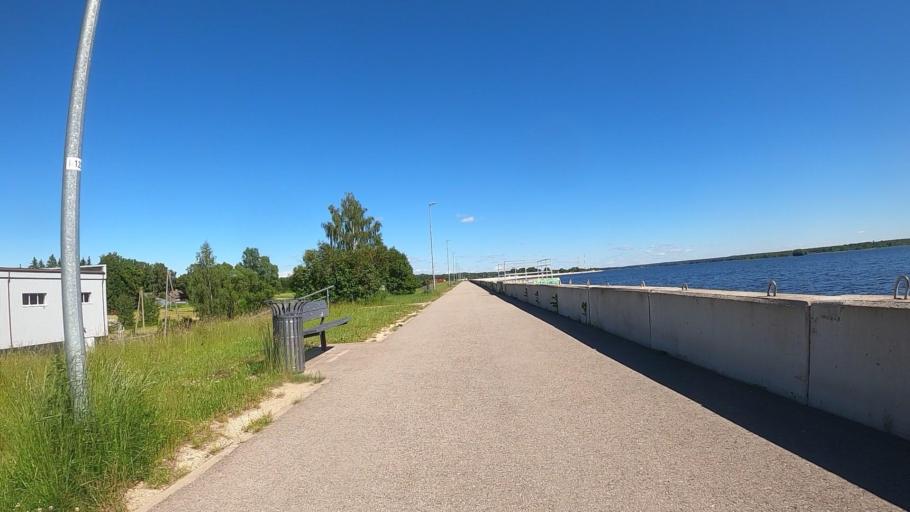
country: LV
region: Ikskile
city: Ikskile
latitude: 56.8420
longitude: 24.4589
